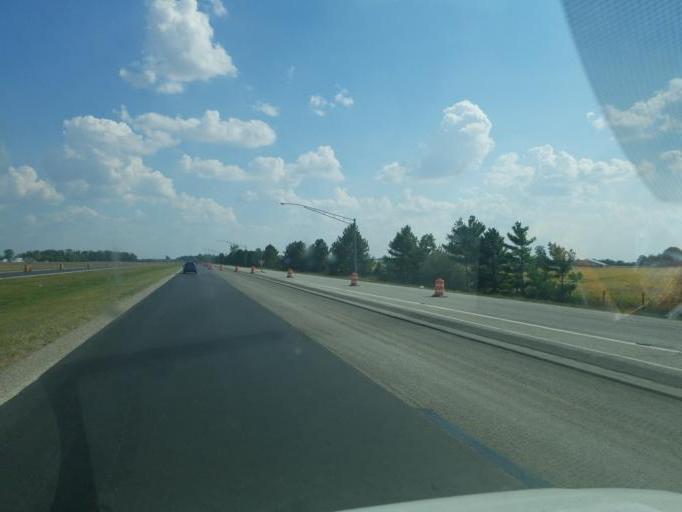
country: US
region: Ohio
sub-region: Van Wert County
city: Convoy
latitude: 40.9079
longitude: -84.6589
